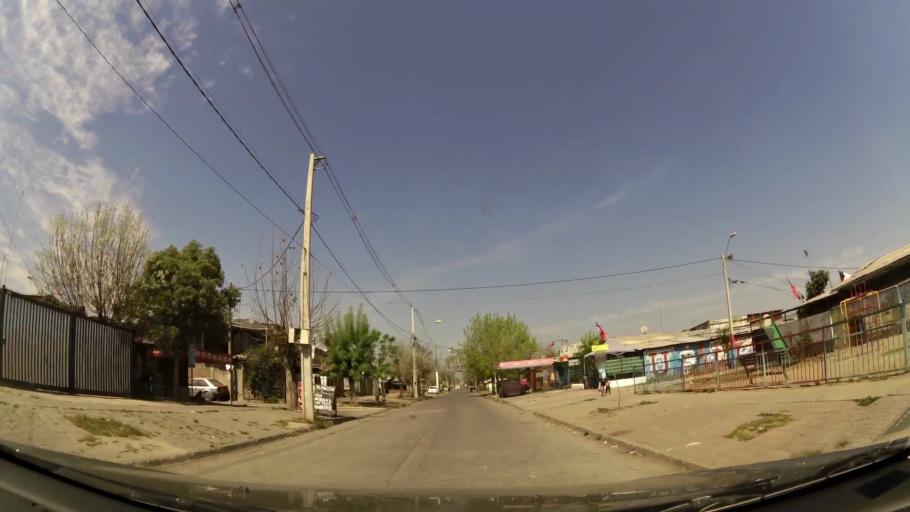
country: CL
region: Santiago Metropolitan
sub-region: Provincia de Santiago
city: La Pintana
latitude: -33.5889
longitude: -70.6130
